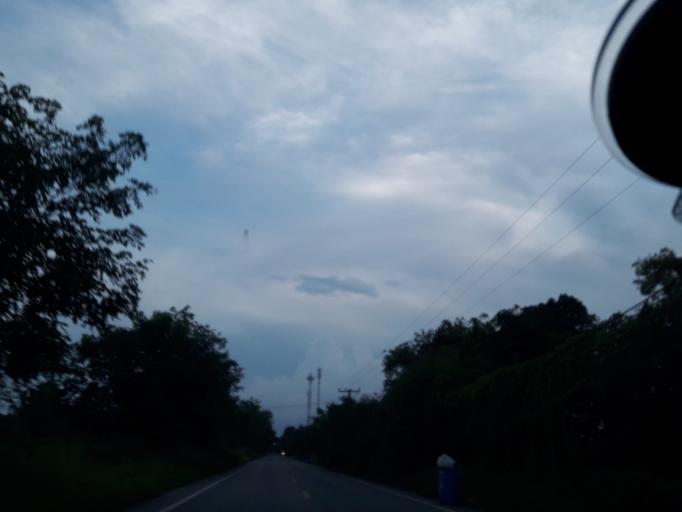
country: TH
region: Pathum Thani
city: Nong Suea
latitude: 14.1113
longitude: 100.8685
